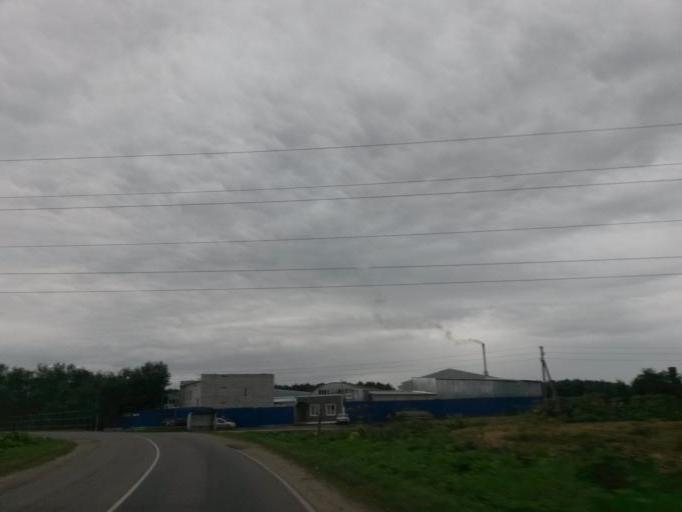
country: RU
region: Moskovskaya
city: Belyye Stolby
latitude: 55.2632
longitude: 37.7637
